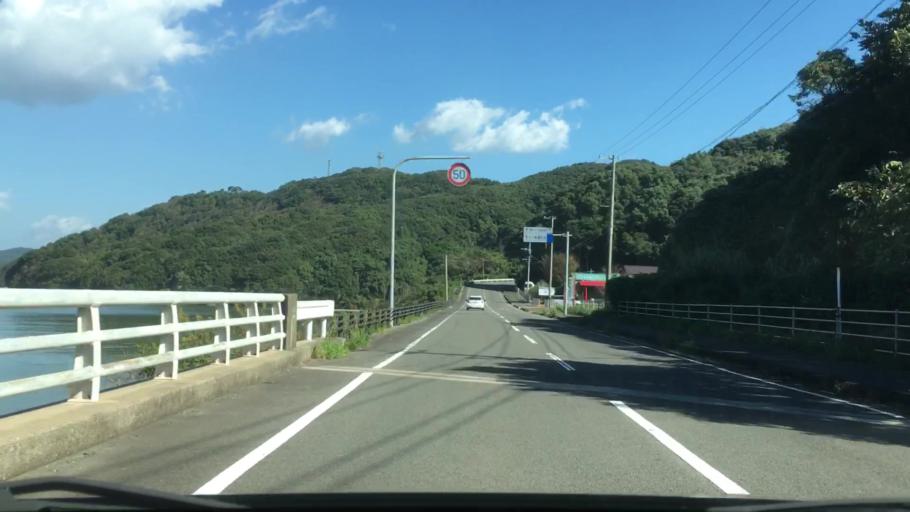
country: JP
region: Nagasaki
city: Sasebo
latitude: 32.9885
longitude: 129.6463
